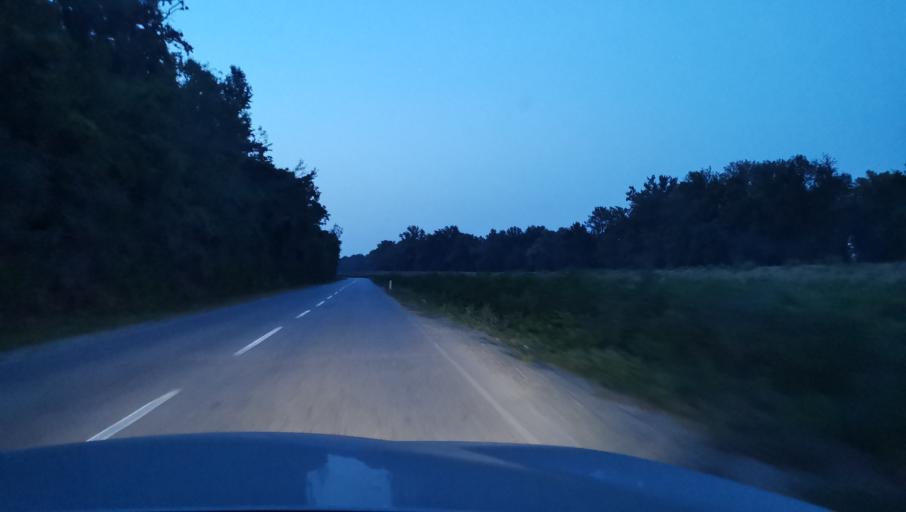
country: RS
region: Central Serbia
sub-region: Belgrade
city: Obrenovac
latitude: 44.6858
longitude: 20.1938
